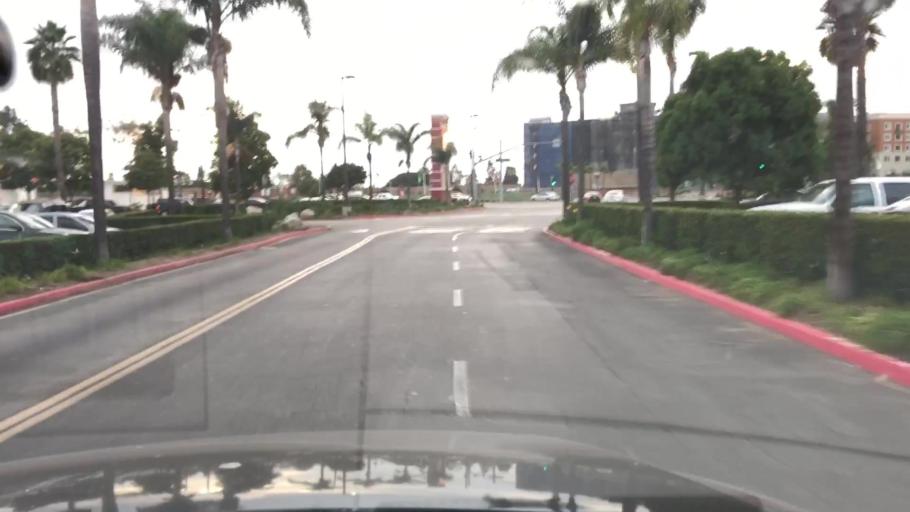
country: US
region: California
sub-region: Ventura County
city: El Rio
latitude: 34.2361
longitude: -119.1791
